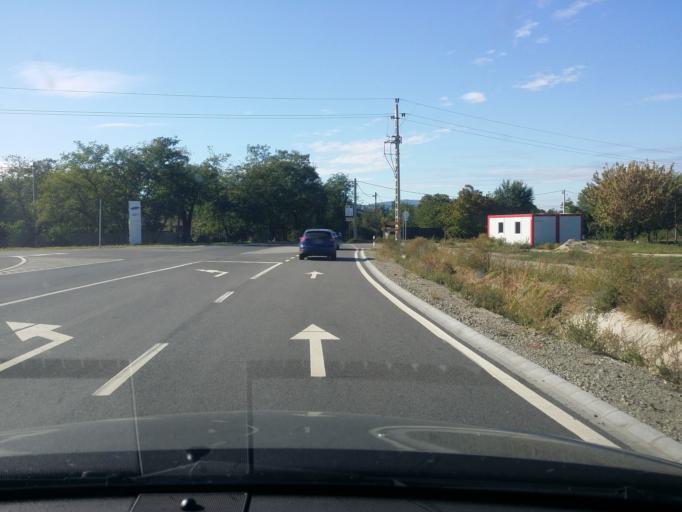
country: HU
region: Pest
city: God
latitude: 47.6827
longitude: 19.1711
